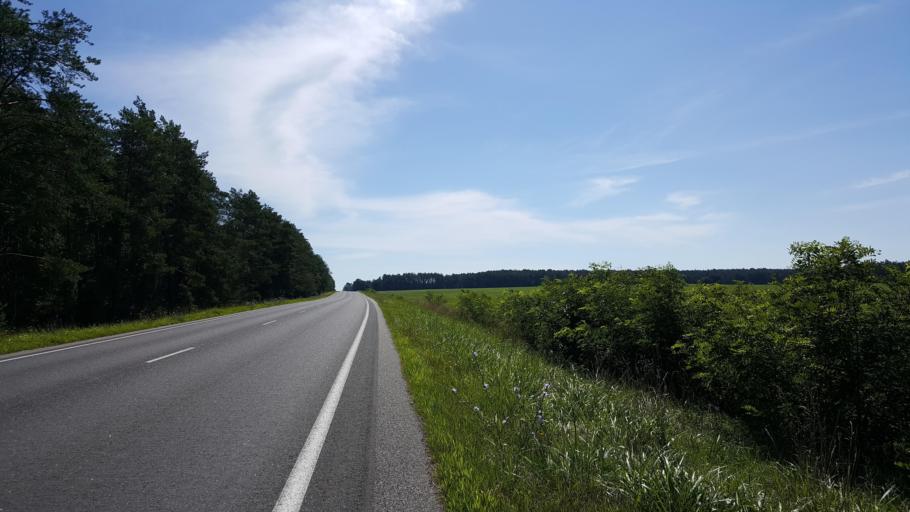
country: BY
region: Brest
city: Kamyanyets
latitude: 52.3976
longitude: 23.9121
